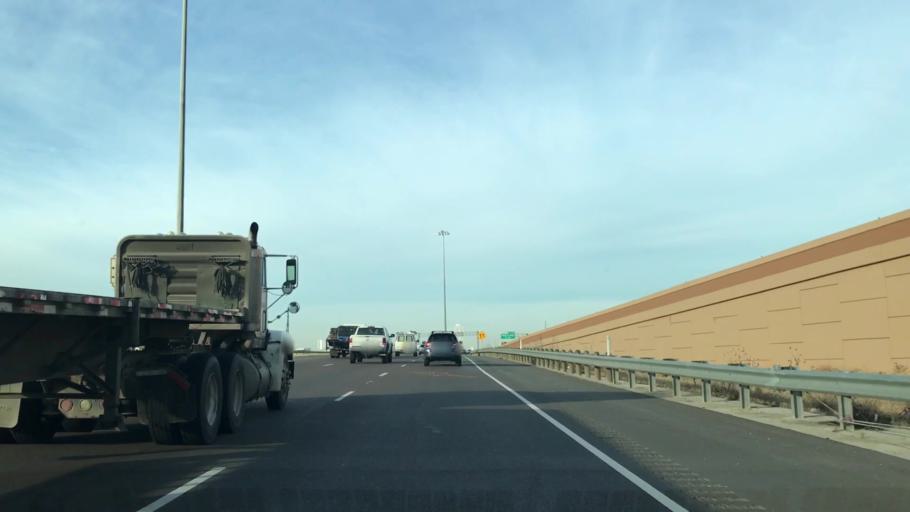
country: US
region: Texas
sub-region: Tarrant County
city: Blue Mound
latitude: 32.8400
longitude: -97.3170
